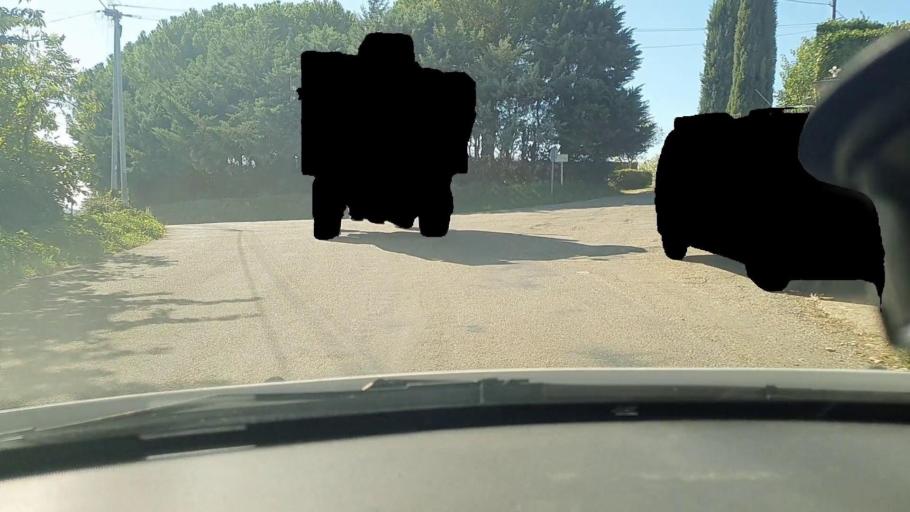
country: FR
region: Languedoc-Roussillon
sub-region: Departement du Gard
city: Saint-Julien-de-Peyrolas
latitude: 44.2749
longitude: 4.5718
